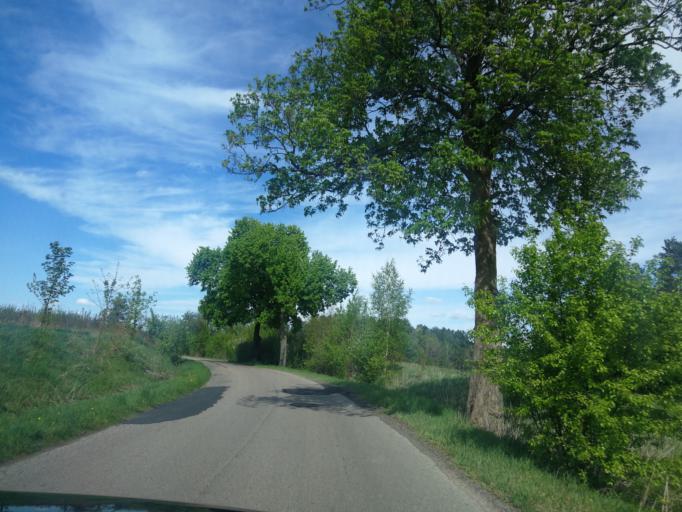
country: PL
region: Warmian-Masurian Voivodeship
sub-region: Powiat ilawski
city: Ilawa
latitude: 53.6809
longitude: 19.6730
